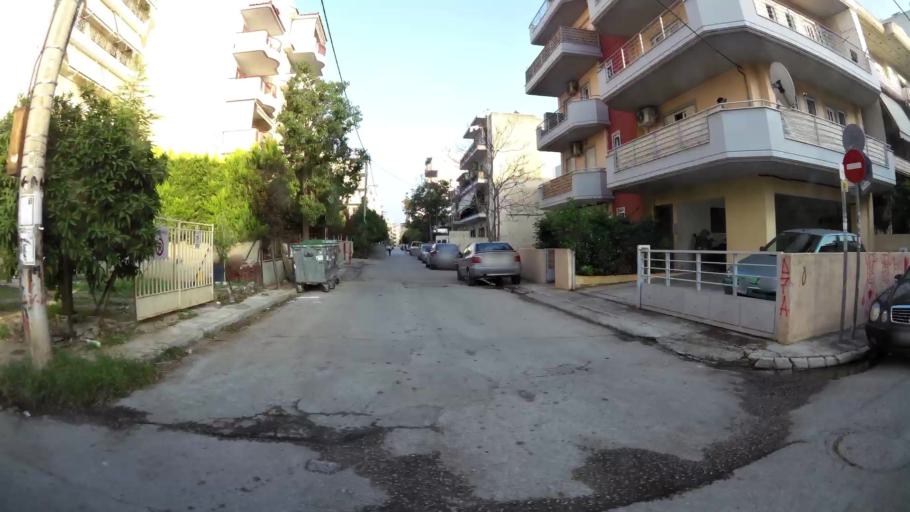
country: GR
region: Attica
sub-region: Nomarchia Anatolikis Attikis
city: Acharnes
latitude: 38.0884
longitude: 23.7347
